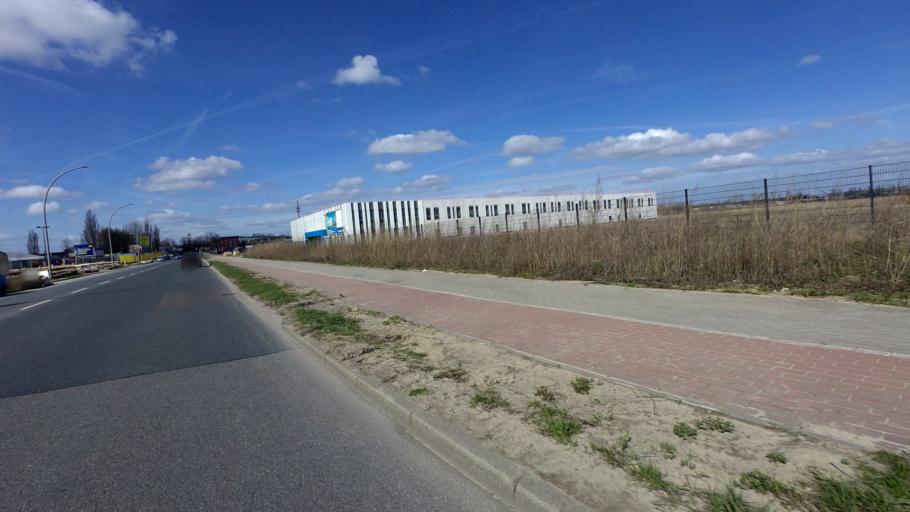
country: DE
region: Berlin
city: Falkenberg
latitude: 52.5548
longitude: 13.5363
